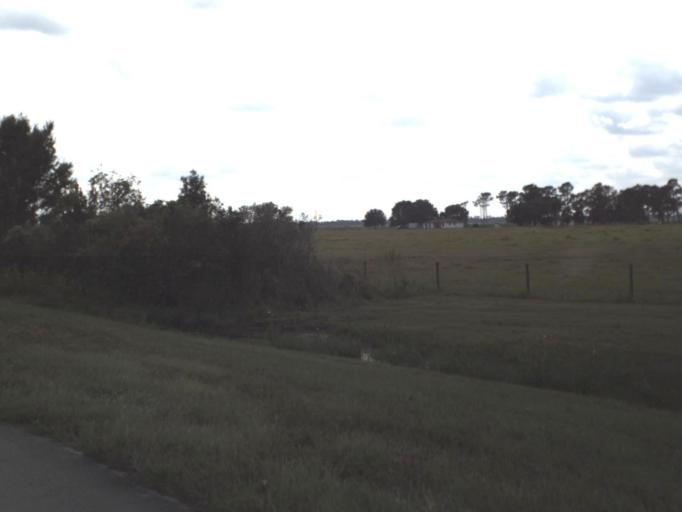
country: US
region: Florida
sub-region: Indian River County
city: Fellsmere
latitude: 27.6208
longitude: -80.8612
